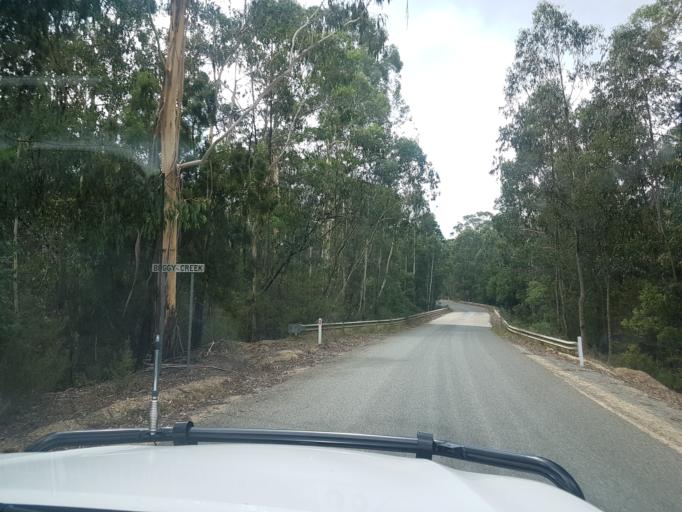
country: AU
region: Victoria
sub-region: East Gippsland
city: Bairnsdale
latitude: -37.6786
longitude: 147.5511
